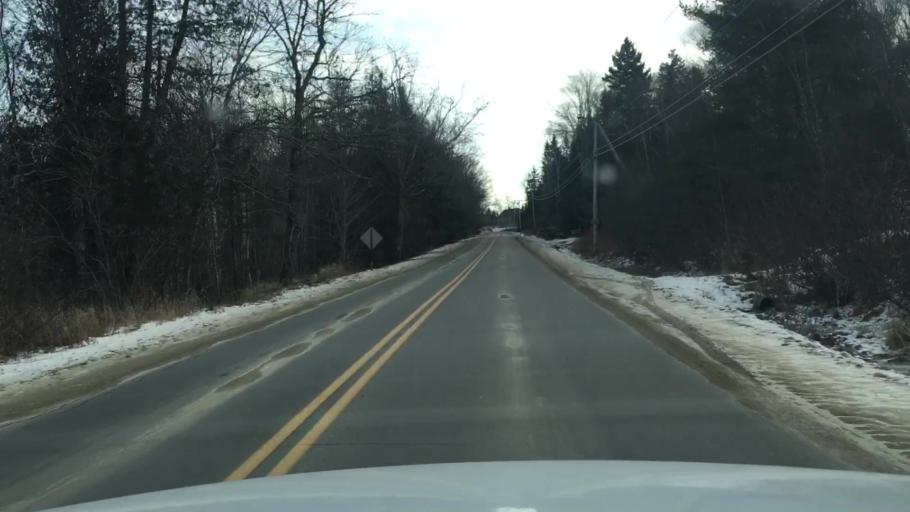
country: US
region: Maine
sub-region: Washington County
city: Jonesport
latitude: 44.6125
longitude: -67.6022
